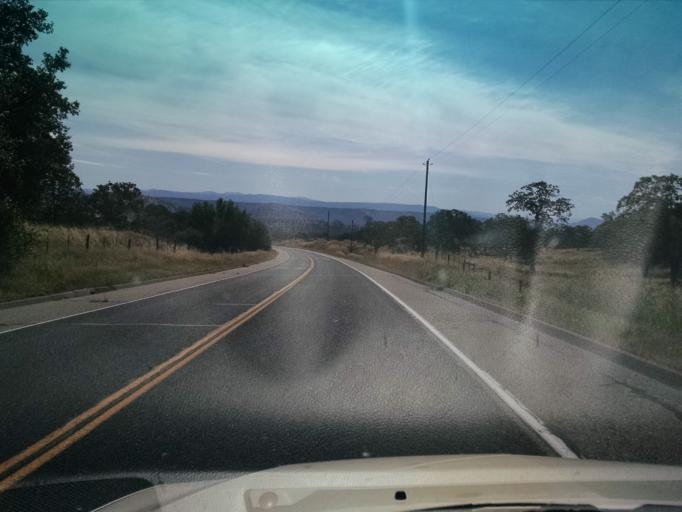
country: US
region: California
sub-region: Madera County
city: Yosemite Lakes
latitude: 37.1209
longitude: -119.7248
